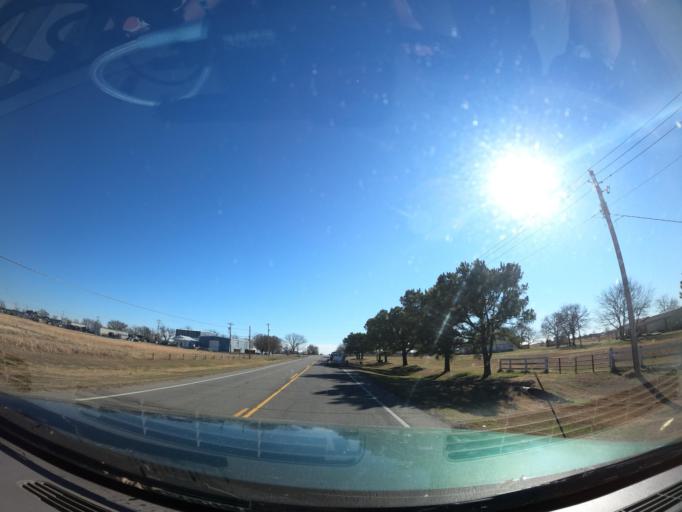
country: US
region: Oklahoma
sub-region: Muskogee County
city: Haskell
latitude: 35.8036
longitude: -95.6725
